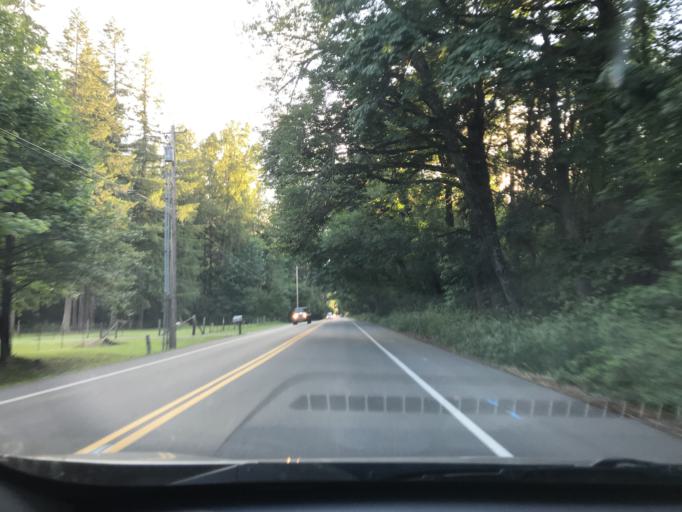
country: US
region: Washington
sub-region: King County
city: Lake Morton-Berrydale
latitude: 47.2977
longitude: -122.0742
